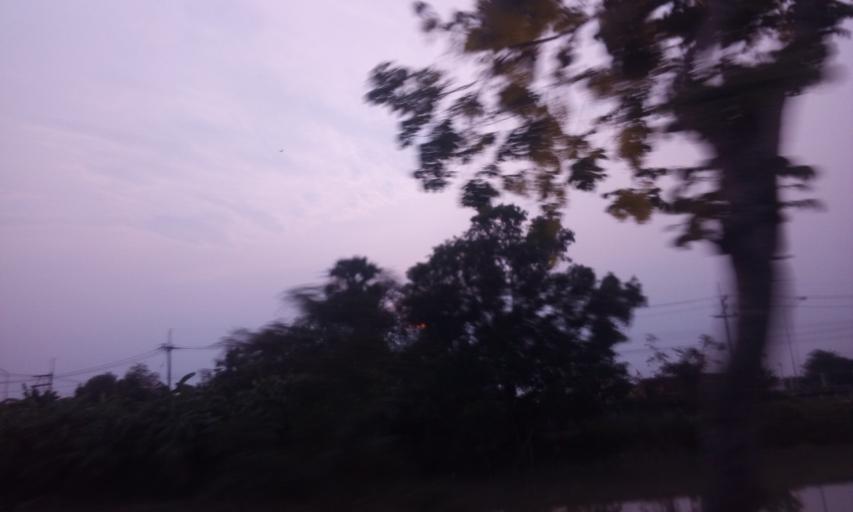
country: TH
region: Pathum Thani
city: Ban Lam Luk Ka
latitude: 13.9851
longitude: 100.8953
